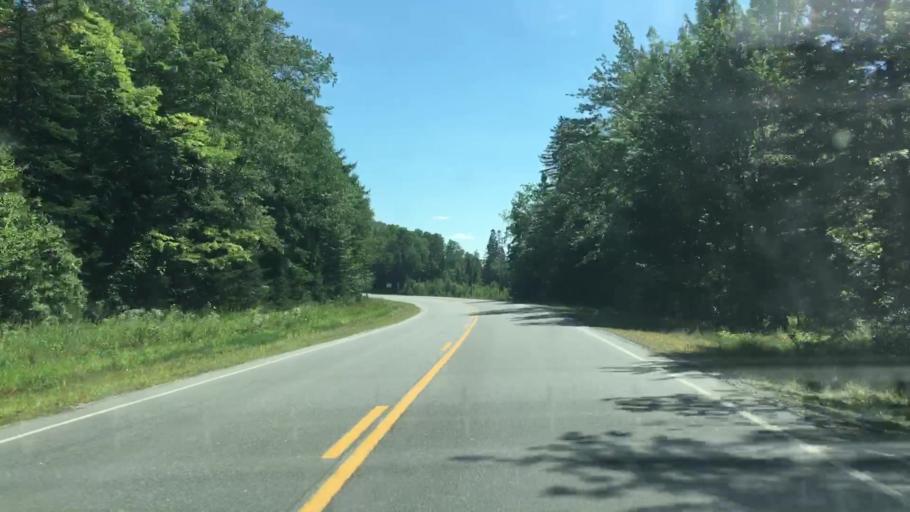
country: US
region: Maine
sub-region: Piscataquis County
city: Milo
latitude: 45.2008
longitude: -68.9068
